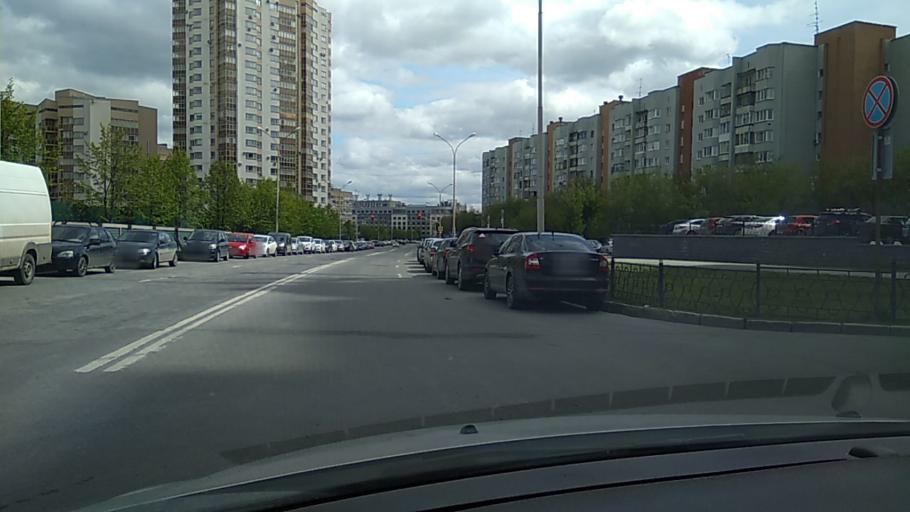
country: RU
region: Sverdlovsk
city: Yekaterinburg
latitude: 56.8419
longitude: 60.5856
